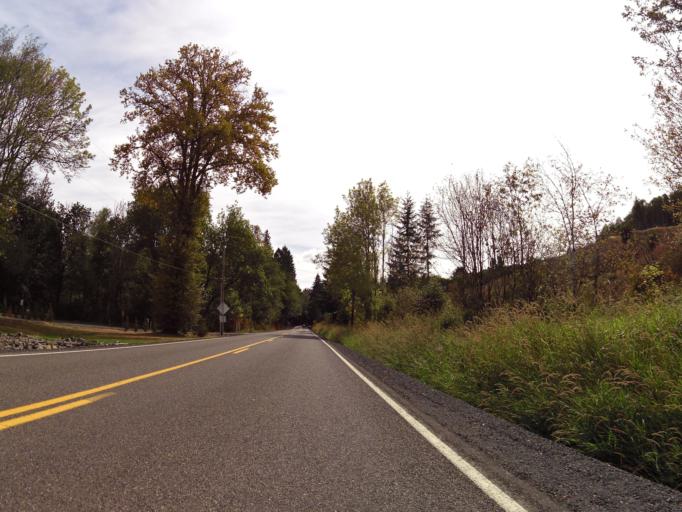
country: US
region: Washington
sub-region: Lewis County
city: Napavine
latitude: 46.5595
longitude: -122.9614
